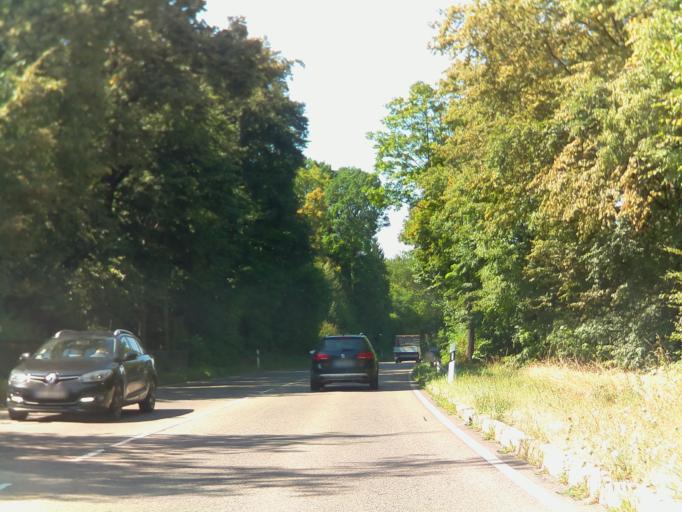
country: DE
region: Baden-Wuerttemberg
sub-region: Regierungsbezirk Stuttgart
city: Gerlingen
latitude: 48.7878
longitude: 9.0524
